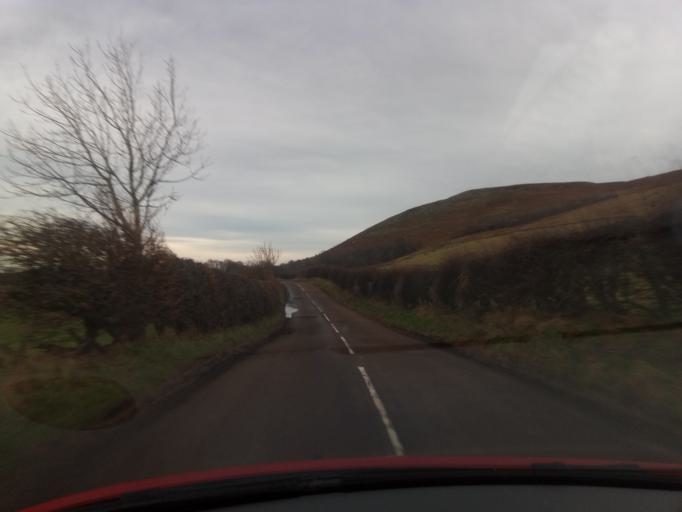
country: GB
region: England
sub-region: Northumberland
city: Kirknewton
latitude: 55.5650
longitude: -2.0965
